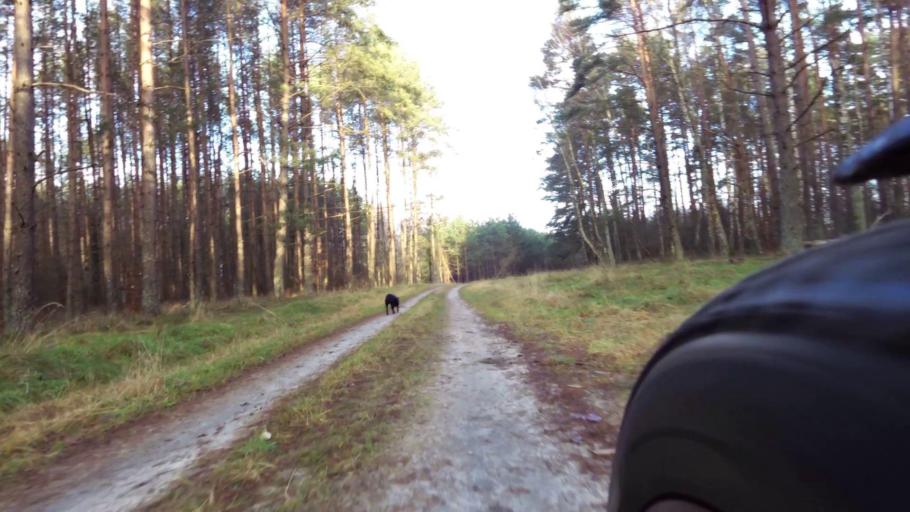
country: PL
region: West Pomeranian Voivodeship
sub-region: Powiat szczecinecki
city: Borne Sulinowo
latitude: 53.6133
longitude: 16.6178
